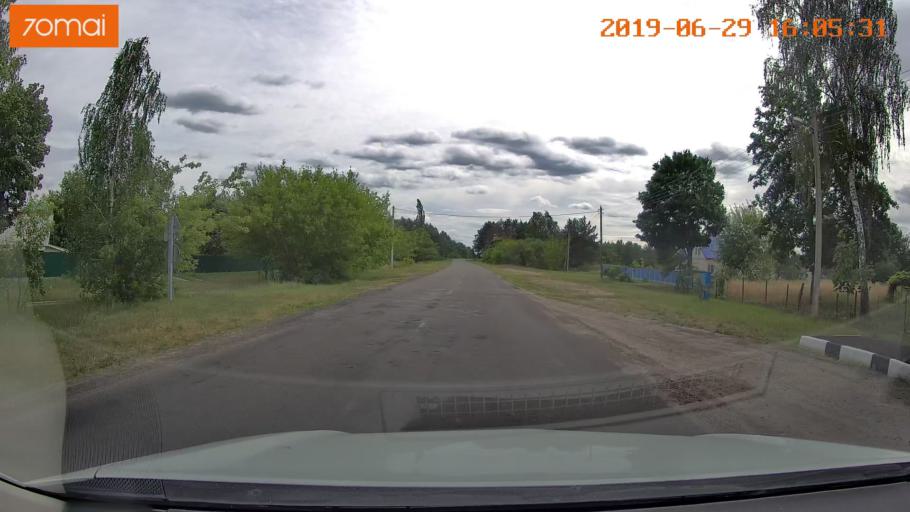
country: BY
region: Brest
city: Luninyets
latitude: 52.2161
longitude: 27.0191
